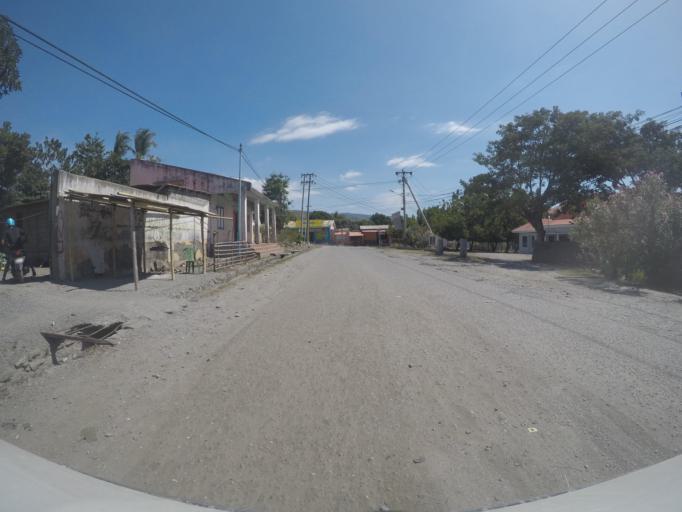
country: TL
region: Liquica
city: Liquica
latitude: -8.5940
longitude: 125.3295
